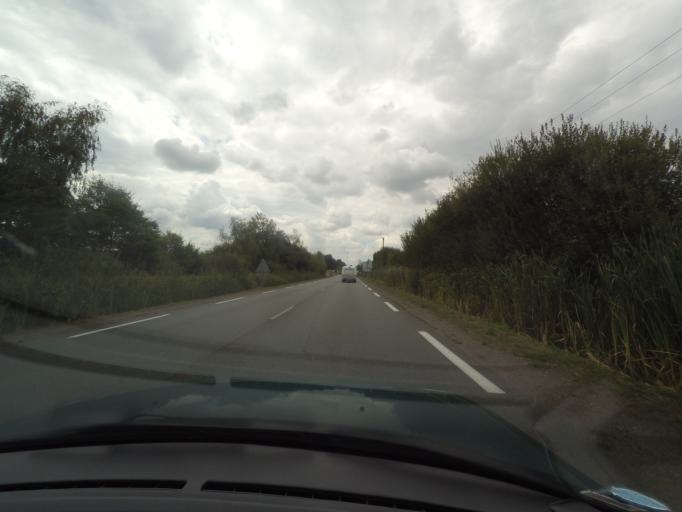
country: FR
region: Poitou-Charentes
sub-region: Departement des Deux-Sevres
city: Chatillon-sur-Thouet
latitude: 46.6650
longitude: -0.2437
